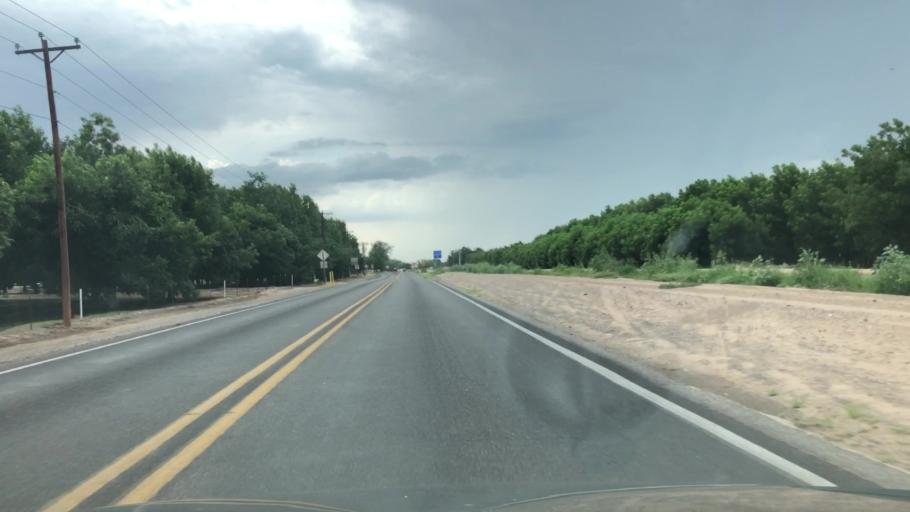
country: US
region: New Mexico
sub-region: Dona Ana County
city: La Union
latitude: 31.9937
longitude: -106.6528
